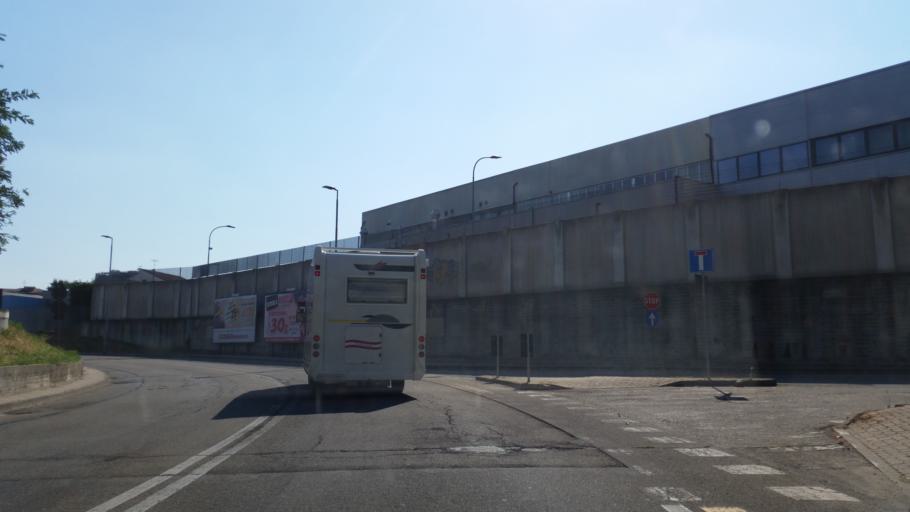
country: IT
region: Piedmont
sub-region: Provincia di Cuneo
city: Alba
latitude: 44.7008
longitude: 8.0285
